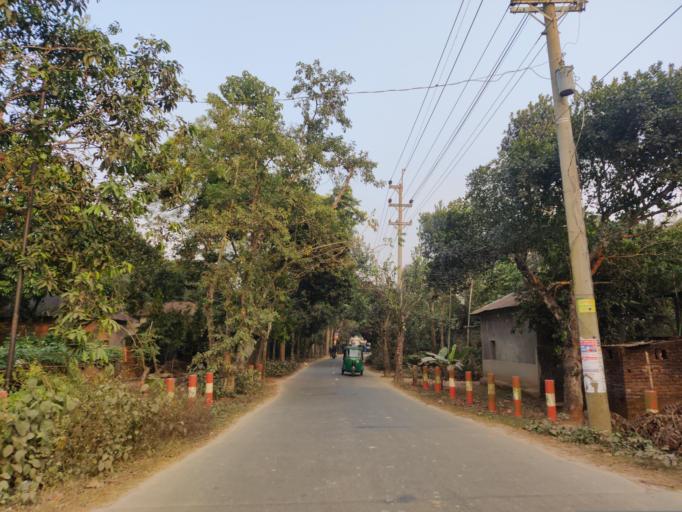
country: BD
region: Dhaka
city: Bajitpur
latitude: 24.1559
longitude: 90.7715
